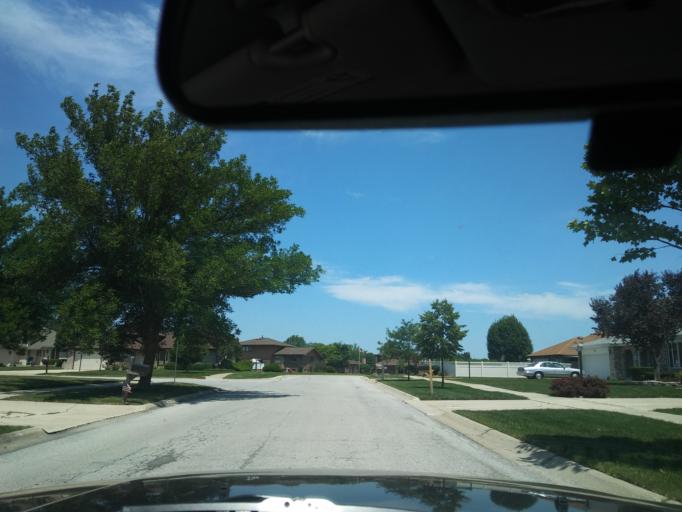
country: US
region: Illinois
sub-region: Cook County
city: Oak Forest
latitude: 41.6044
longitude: -87.7721
